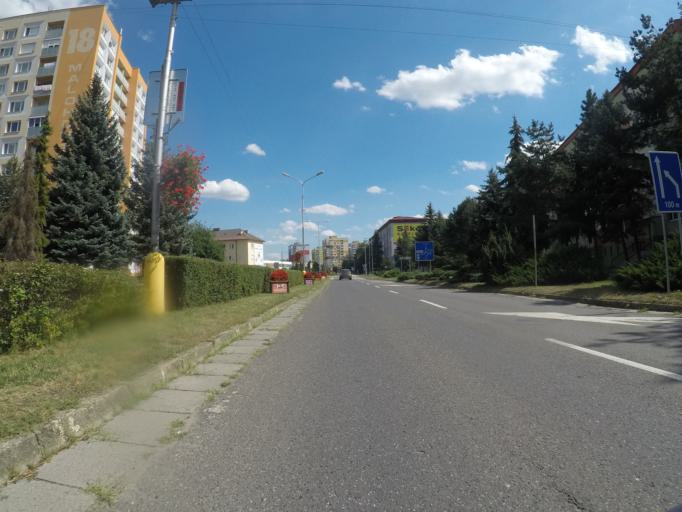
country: SK
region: Banskobystricky
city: Rimavska Sobota
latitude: 48.3831
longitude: 20.0133
